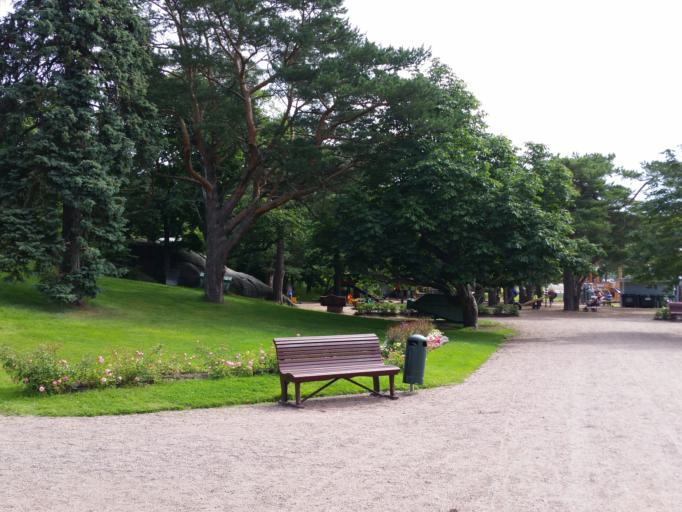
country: FI
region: Uusimaa
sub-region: Raaseporin
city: Hanko
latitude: 59.8233
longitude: 22.9701
